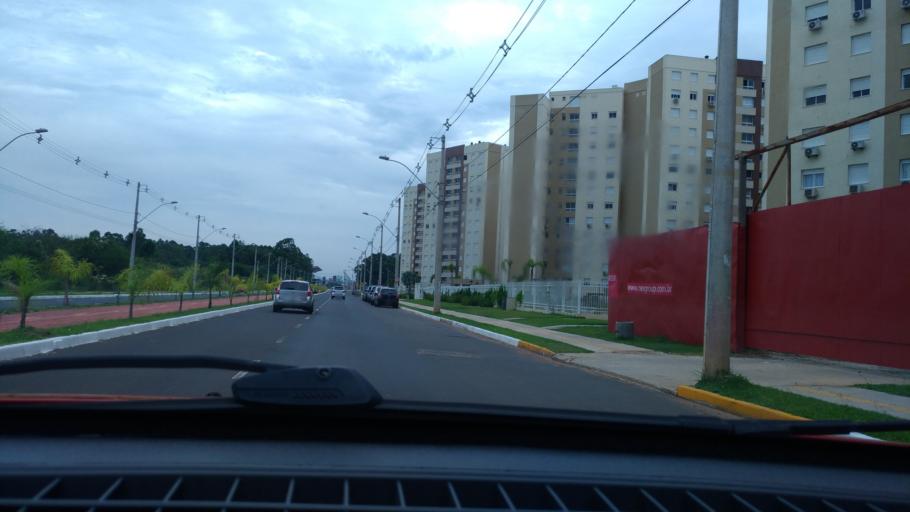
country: BR
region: Rio Grande do Sul
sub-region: Canoas
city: Canoas
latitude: -29.9075
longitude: -51.1651
